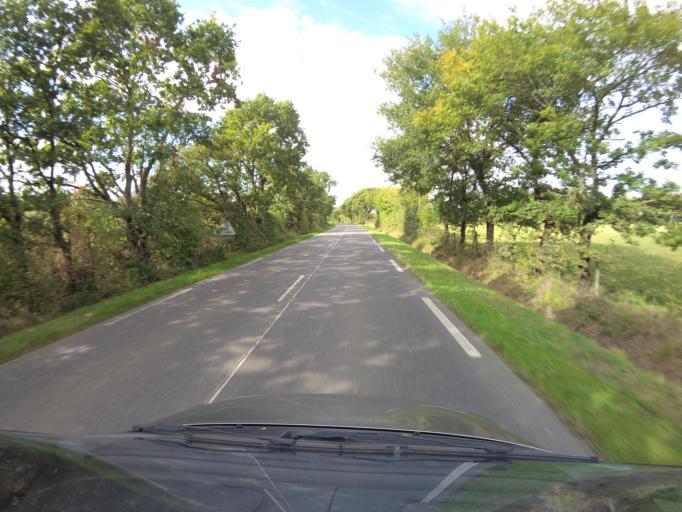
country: FR
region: Pays de la Loire
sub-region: Departement de la Loire-Atlantique
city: Plesse
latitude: 47.5100
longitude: -1.8787
